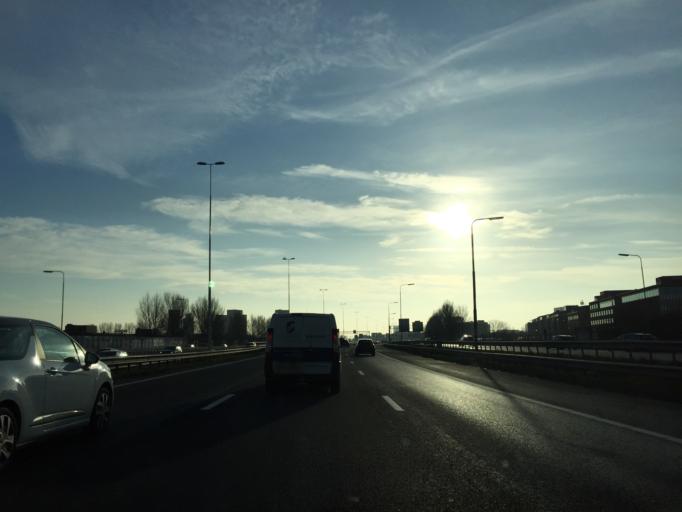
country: NL
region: South Holland
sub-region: Gemeente Rotterdam
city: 's-Gravenland
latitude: 51.9262
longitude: 4.5382
